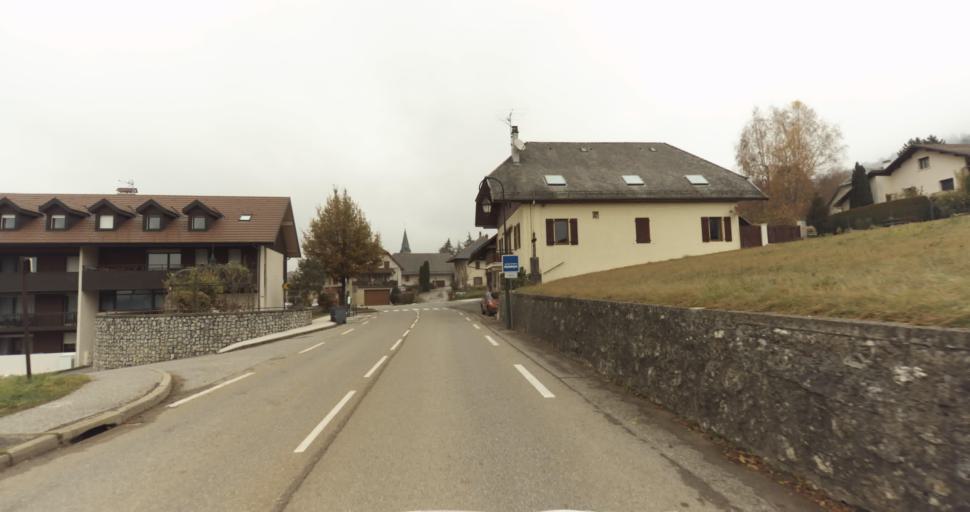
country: FR
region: Rhone-Alpes
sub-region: Departement de la Haute-Savoie
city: Gruffy
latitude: 45.7862
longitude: 6.0543
